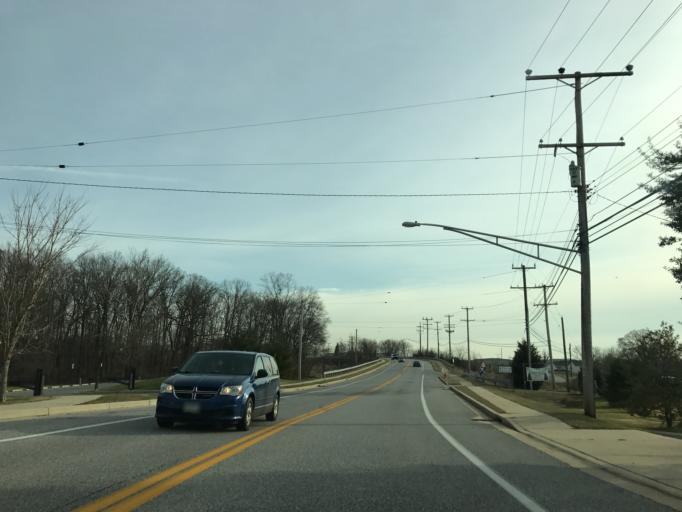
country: US
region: Maryland
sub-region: Baltimore County
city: White Marsh
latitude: 39.3912
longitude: -76.4402
